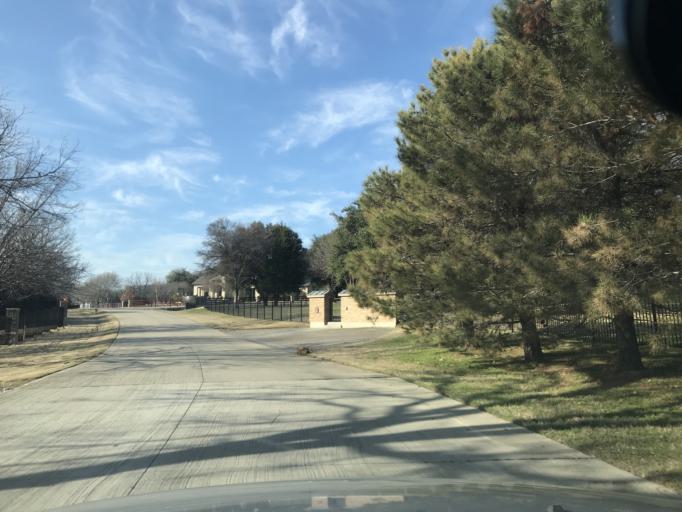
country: US
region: Texas
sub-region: Collin County
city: Frisco
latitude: 33.0960
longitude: -96.8307
